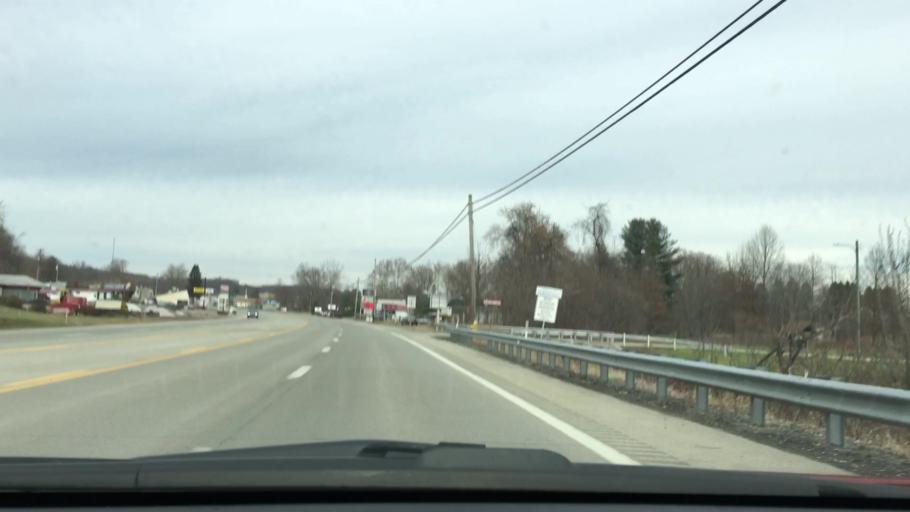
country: US
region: Pennsylvania
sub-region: Fayette County
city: Perryopolis
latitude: 40.0787
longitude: -79.7602
